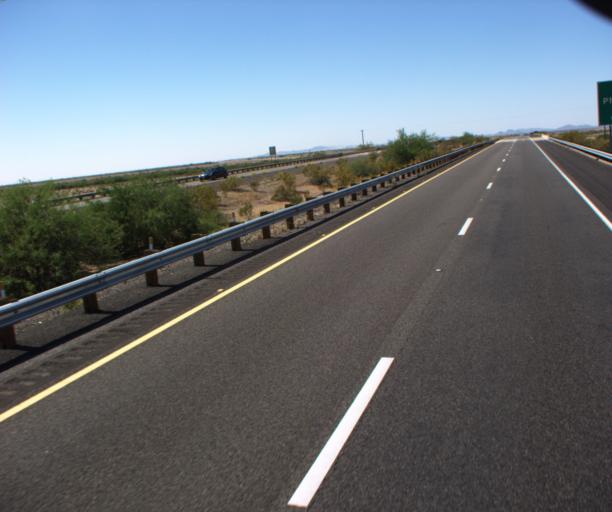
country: US
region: Arizona
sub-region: Maricopa County
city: Gila Bend
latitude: 32.9366
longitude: -112.7205
